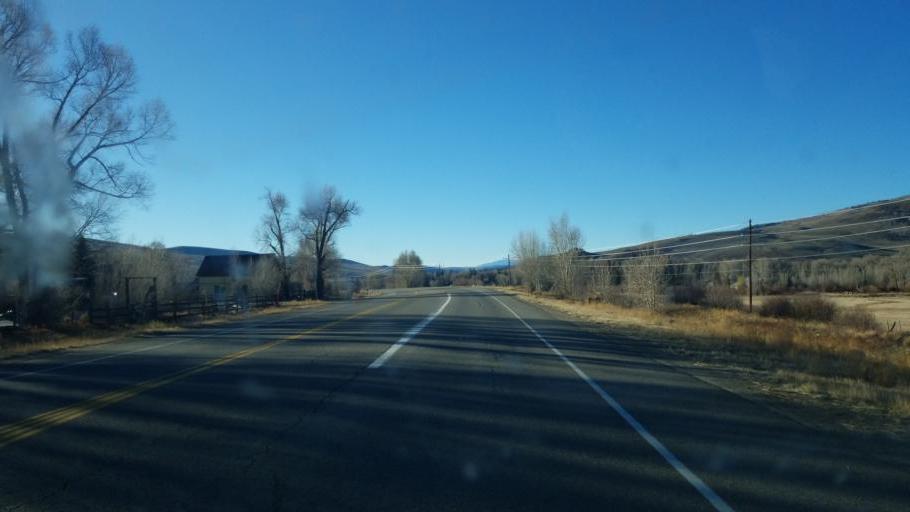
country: US
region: Colorado
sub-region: Gunnison County
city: Crested Butte
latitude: 38.7408
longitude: -106.8567
